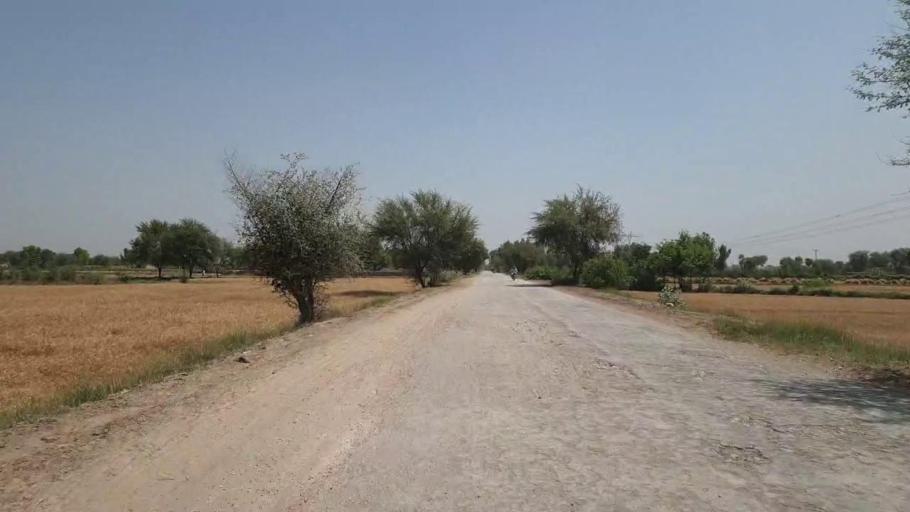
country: PK
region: Sindh
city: Adilpur
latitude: 27.8401
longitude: 69.2655
